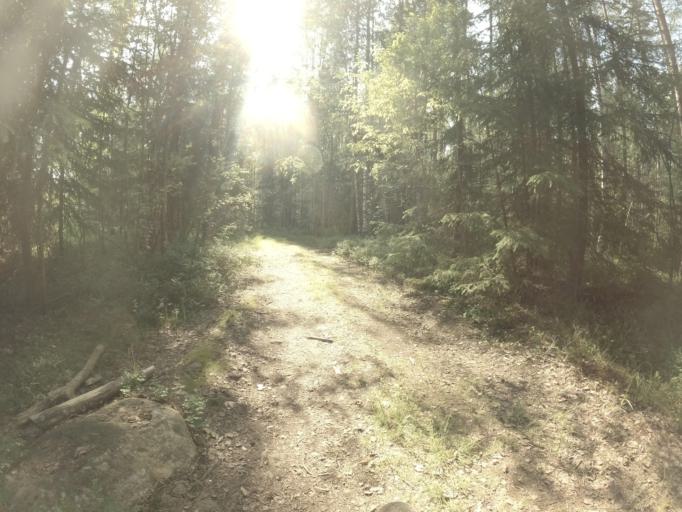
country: RU
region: Leningrad
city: Yakovlevo
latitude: 60.4490
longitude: 29.2478
